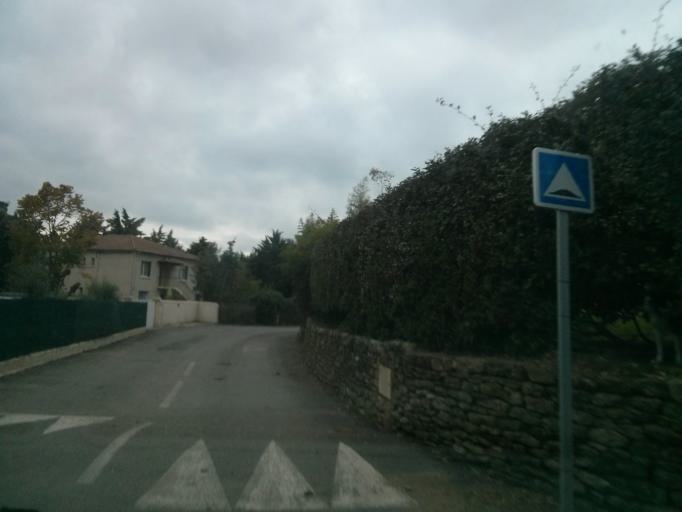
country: FR
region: Languedoc-Roussillon
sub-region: Departement du Gard
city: Aubais
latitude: 43.7561
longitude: 4.1431
